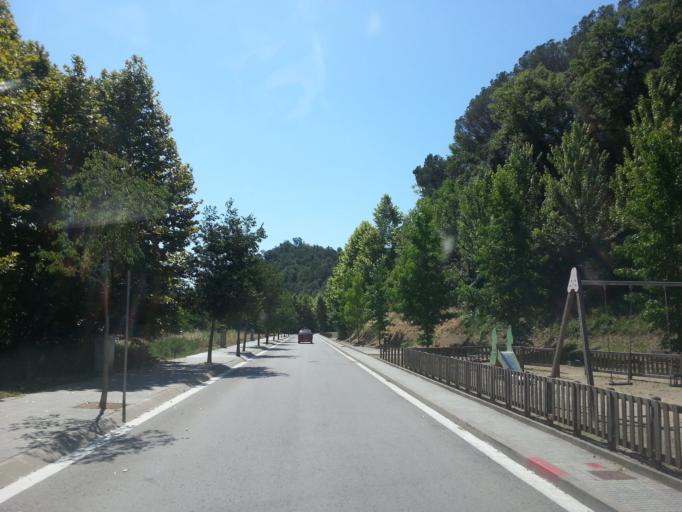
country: ES
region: Catalonia
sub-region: Provincia de Barcelona
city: Campins
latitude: 41.7299
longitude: 2.5032
